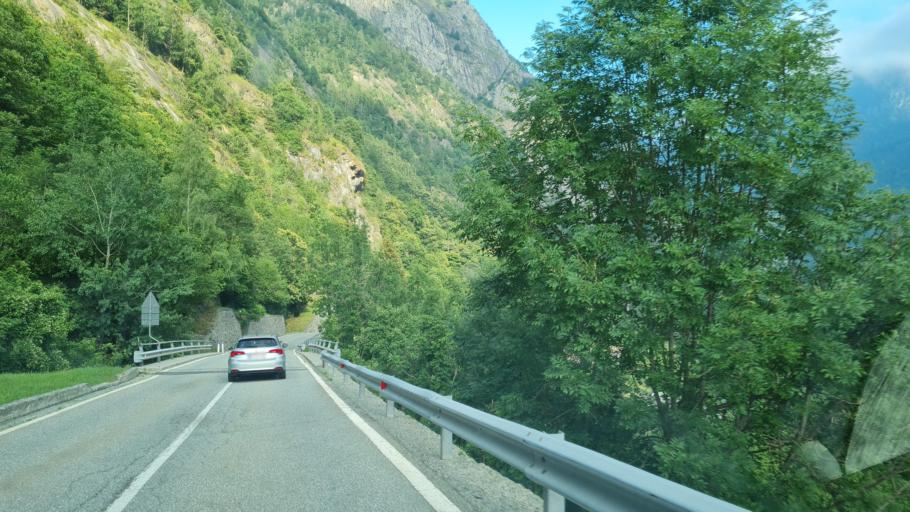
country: IT
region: Aosta Valley
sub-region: Valle d'Aosta
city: Pont-Bozet
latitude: 45.6176
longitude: 7.6715
